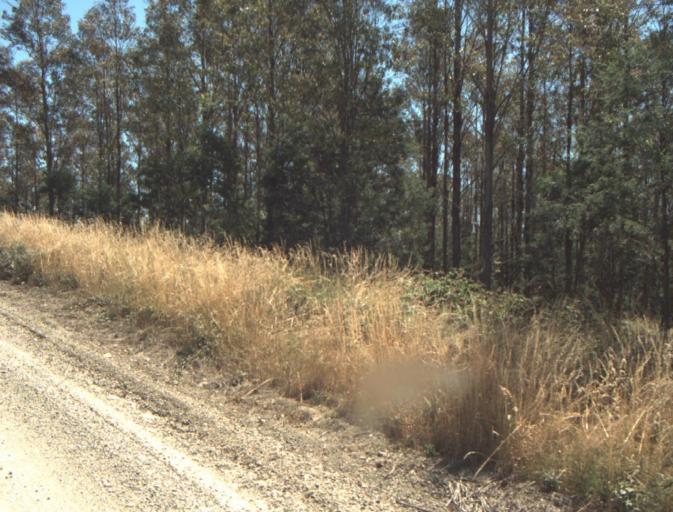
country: AU
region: Tasmania
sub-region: Dorset
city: Scottsdale
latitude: -41.3302
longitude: 147.4374
